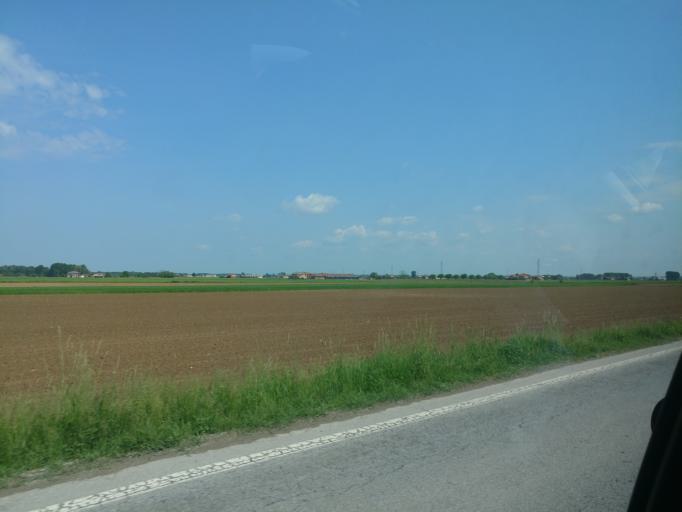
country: IT
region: Piedmont
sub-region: Provincia di Torino
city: Cavour
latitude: 44.7595
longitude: 7.3999
